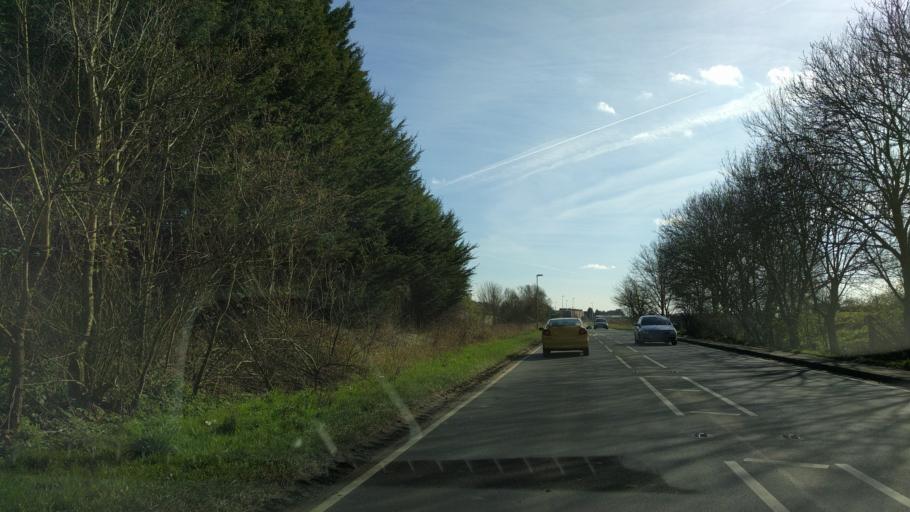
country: GB
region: England
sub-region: Cambridgeshire
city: Chatteris
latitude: 52.4628
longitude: 0.0430
